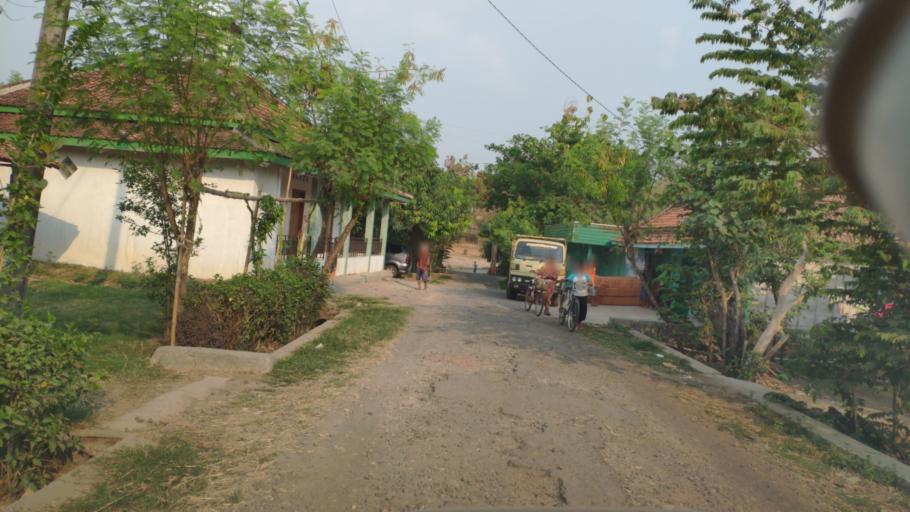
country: ID
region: Central Java
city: Plumbon
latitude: -7.0510
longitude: 111.2845
